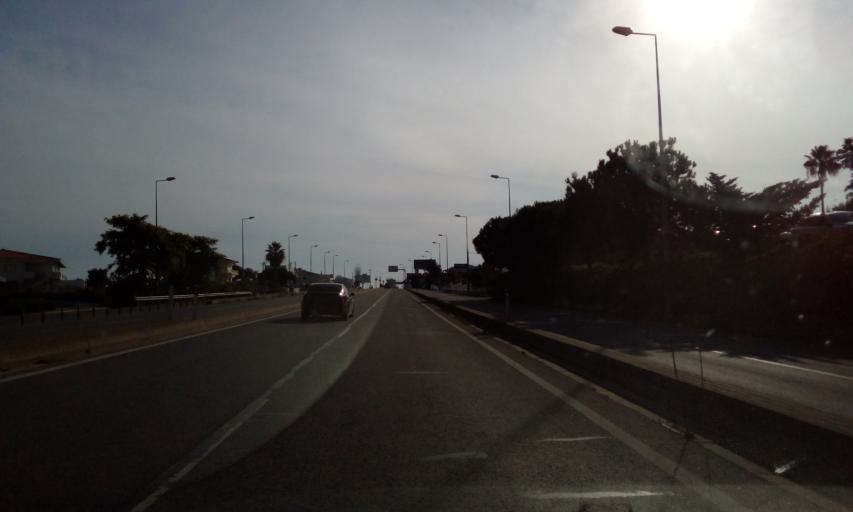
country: PT
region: Faro
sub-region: Faro
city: Faro
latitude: 37.0274
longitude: -7.9693
